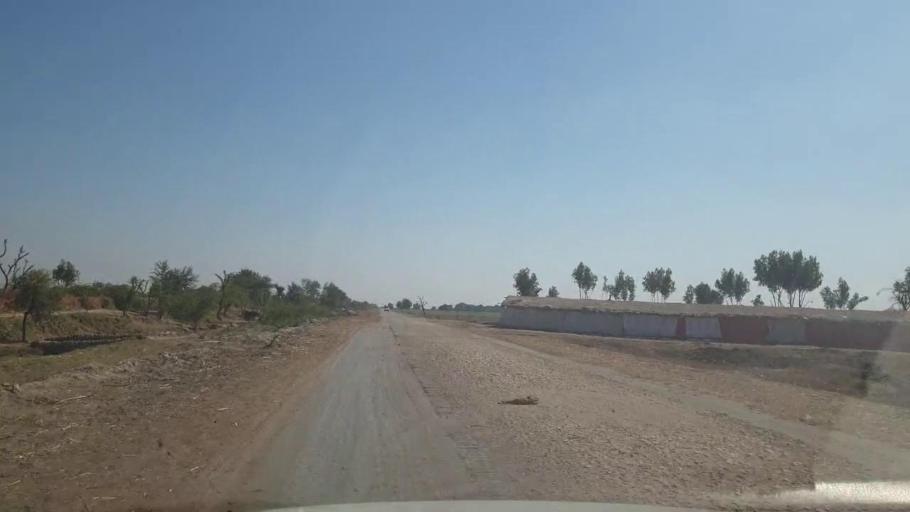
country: PK
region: Sindh
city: Mirpur Khas
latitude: 25.4695
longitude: 69.1771
